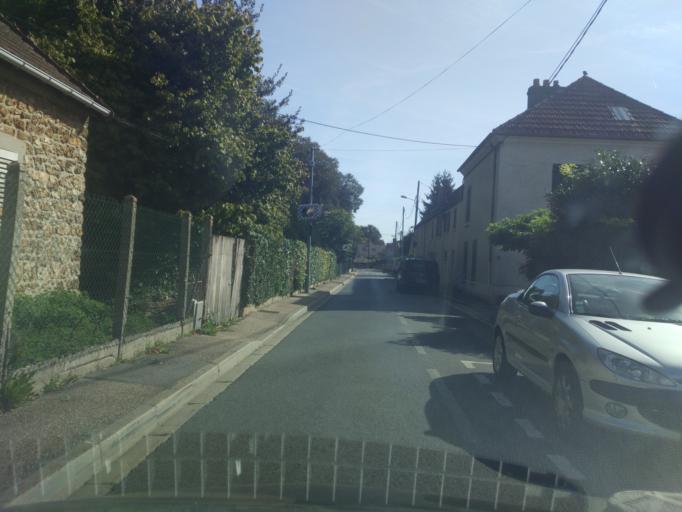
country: FR
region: Ile-de-France
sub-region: Departement de l'Essonne
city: Limours
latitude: 48.6469
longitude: 2.0809
